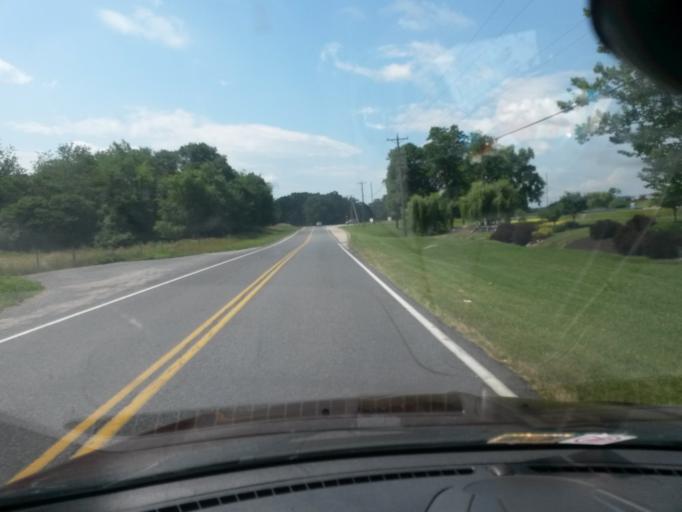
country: US
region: Virginia
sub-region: Augusta County
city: Stuarts Draft
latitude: 37.9286
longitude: -79.2270
